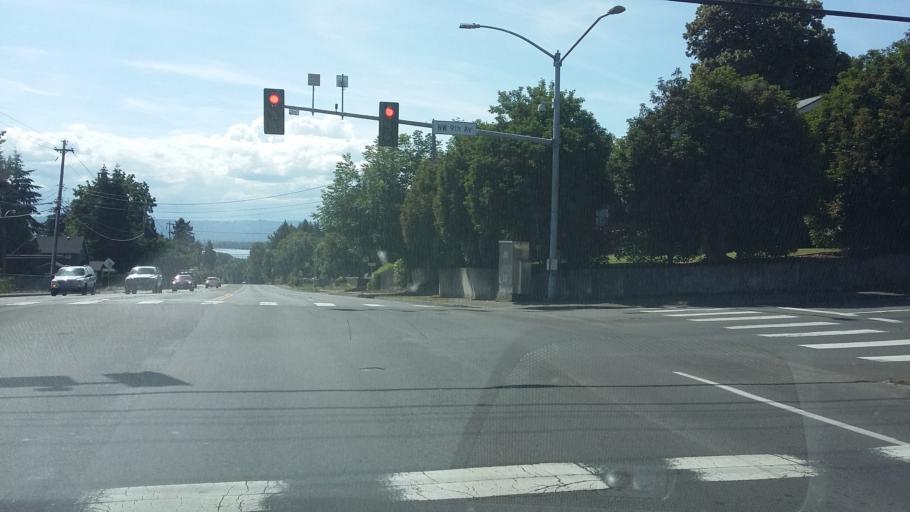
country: US
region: Washington
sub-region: Clark County
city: Lake Shore
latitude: 45.6786
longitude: -122.6795
